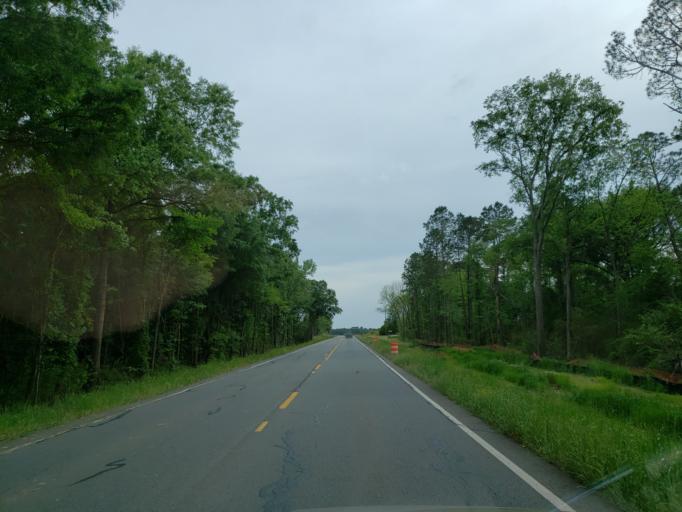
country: US
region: Georgia
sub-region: Macon County
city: Marshallville
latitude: 32.3738
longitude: -83.8904
